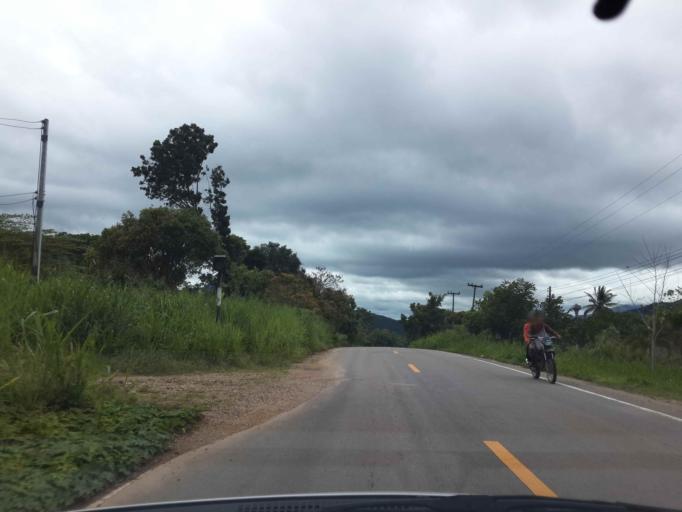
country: TH
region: Ratchaburi
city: Suan Phueng
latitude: 13.6769
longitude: 99.2010
